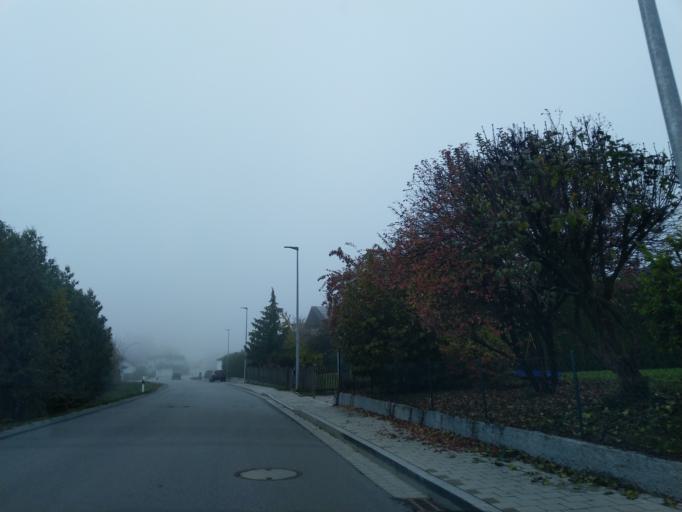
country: DE
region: Bavaria
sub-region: Lower Bavaria
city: Hengersberg
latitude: 48.7726
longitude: 13.0613
